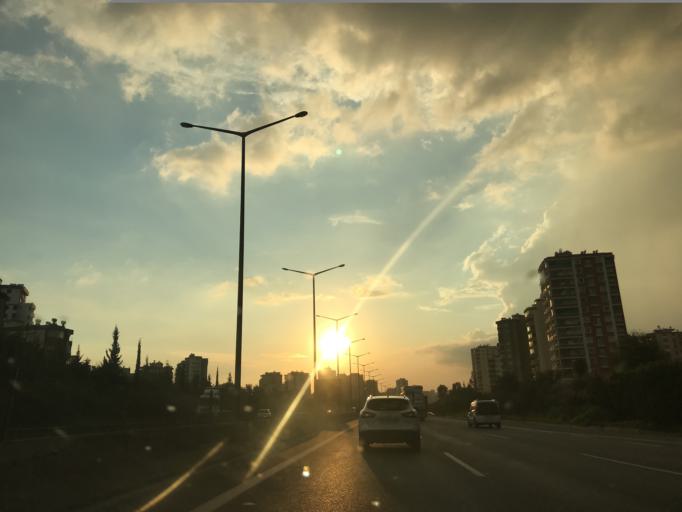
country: TR
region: Adana
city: Seyhan
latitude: 37.0315
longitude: 35.2848
